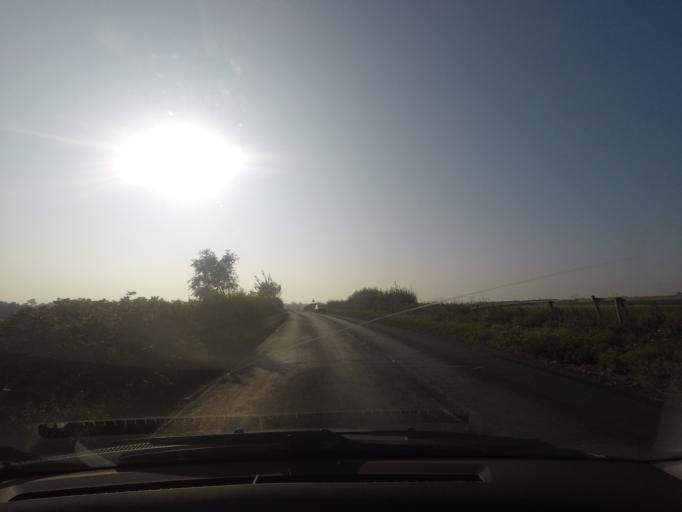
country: GB
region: England
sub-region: City and Borough of Leeds
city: Walton
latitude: 54.0144
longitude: -1.3103
